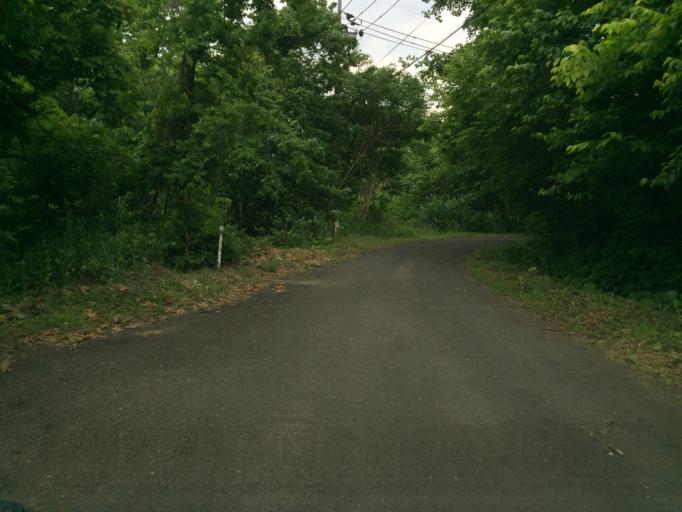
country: JP
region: Fukushima
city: Fukushima-shi
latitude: 37.7145
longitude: 140.3345
